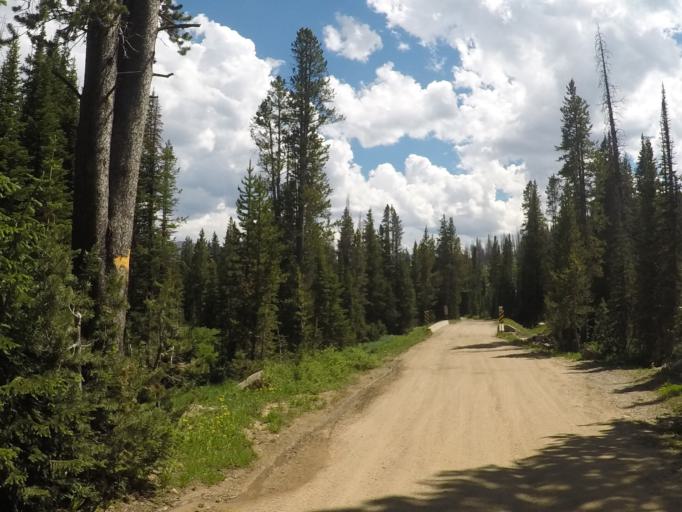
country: US
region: Montana
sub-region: Stillwater County
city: Absarokee
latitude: 45.0397
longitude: -109.9077
